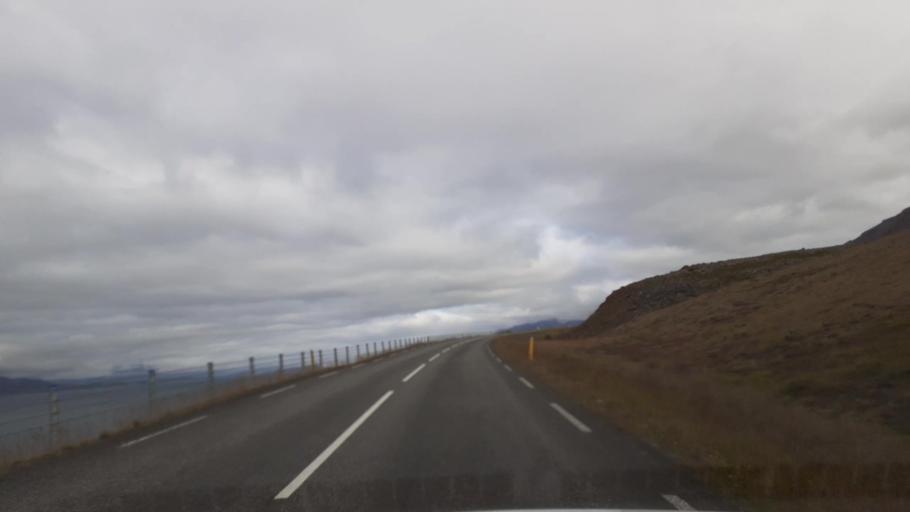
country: IS
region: Northeast
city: Akureyri
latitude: 65.8254
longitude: -18.0563
